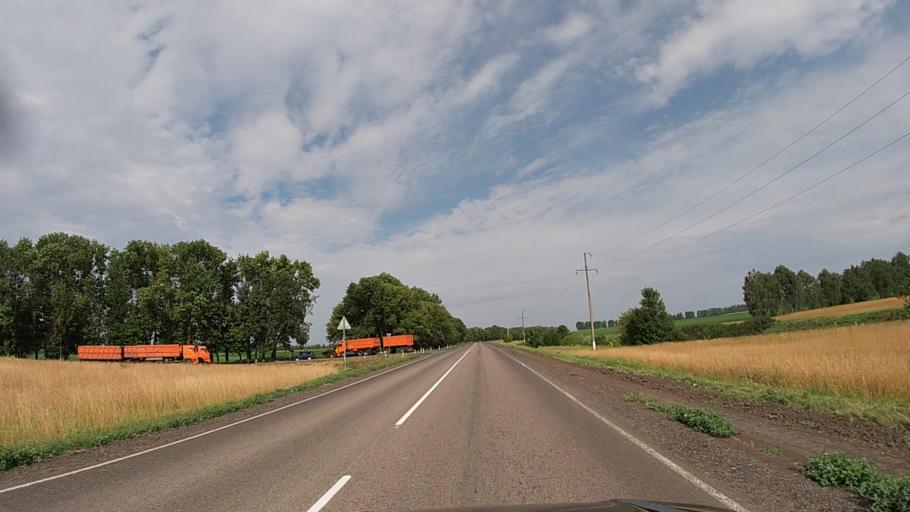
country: RU
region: Belgorod
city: Krasnaya Yaruga
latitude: 50.8011
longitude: 35.5622
